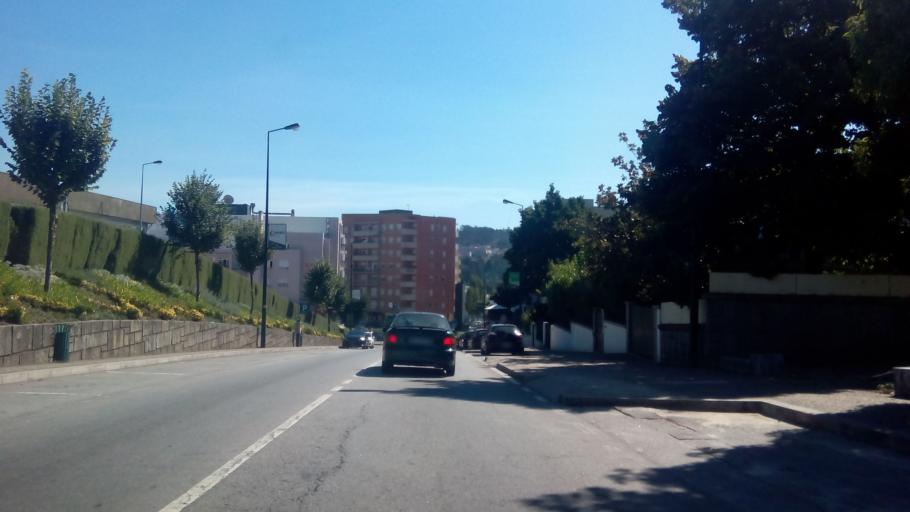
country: PT
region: Porto
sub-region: Paredes
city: Paredes
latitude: 41.2039
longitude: -8.3321
